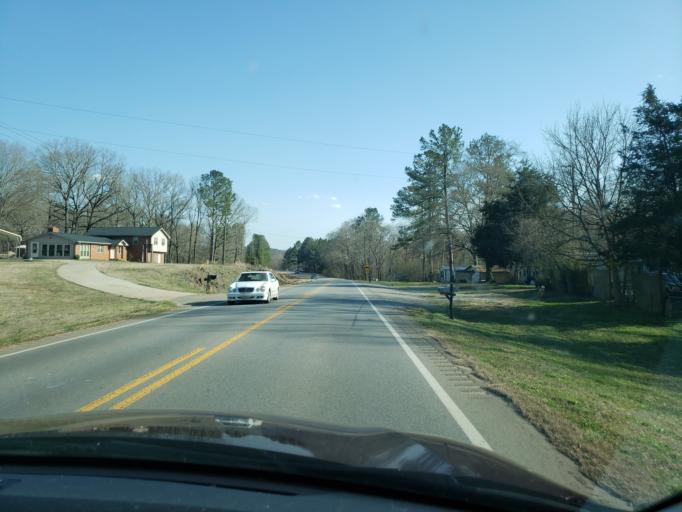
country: US
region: Alabama
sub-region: Cleburne County
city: Heflin
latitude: 33.5190
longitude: -85.6346
